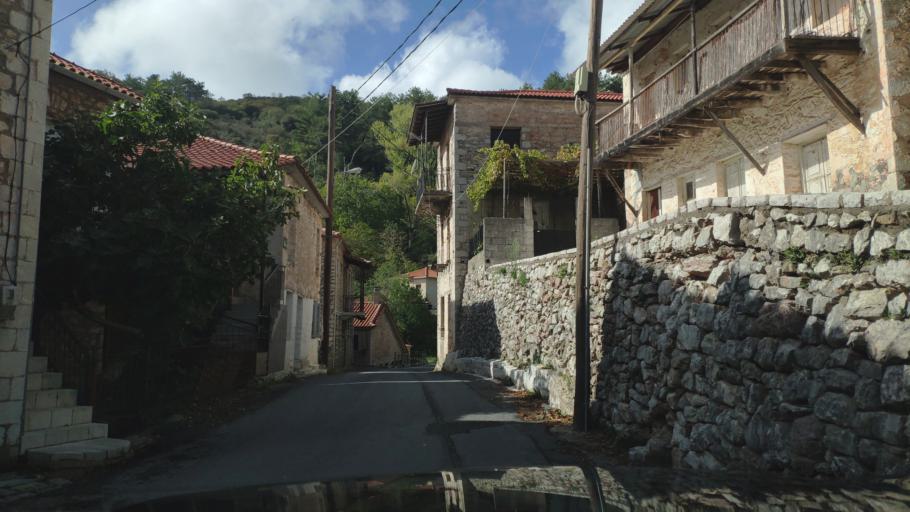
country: GR
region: Peloponnese
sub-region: Nomos Arkadias
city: Dimitsana
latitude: 37.5904
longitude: 22.0236
